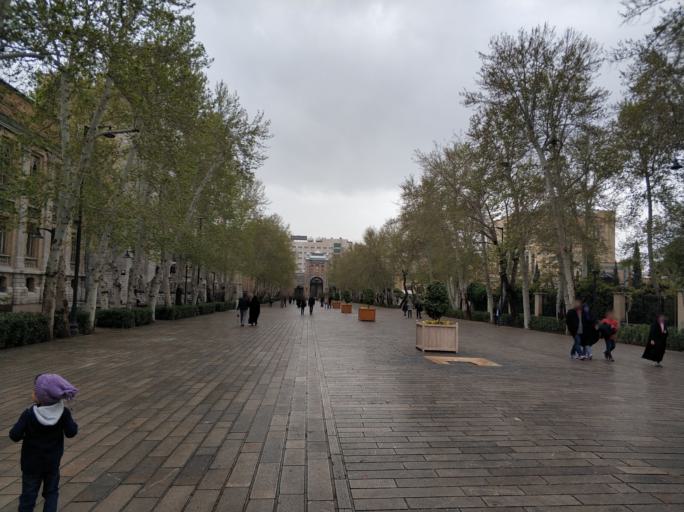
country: IR
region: Tehran
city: Tehran
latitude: 35.6883
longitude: 51.4169
